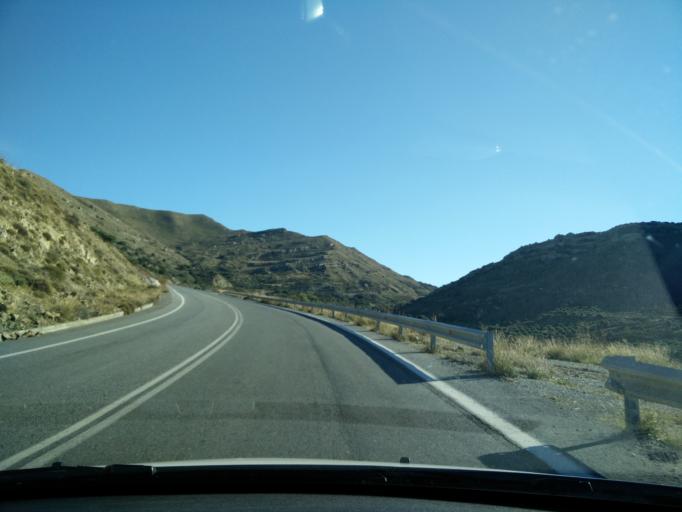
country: GR
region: Crete
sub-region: Nomos Irakleiou
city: Arkalochori
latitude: 35.0663
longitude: 25.3548
